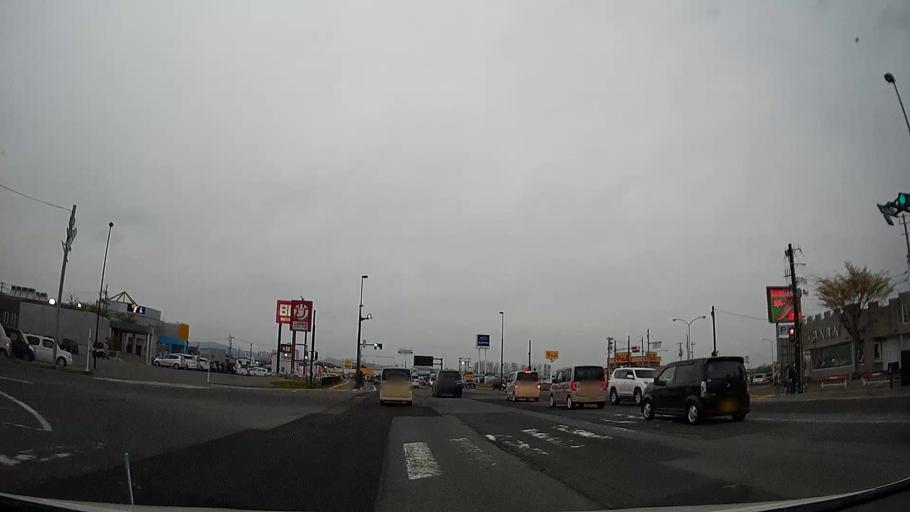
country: JP
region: Aomori
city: Aomori Shi
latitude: 40.8322
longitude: 140.7015
